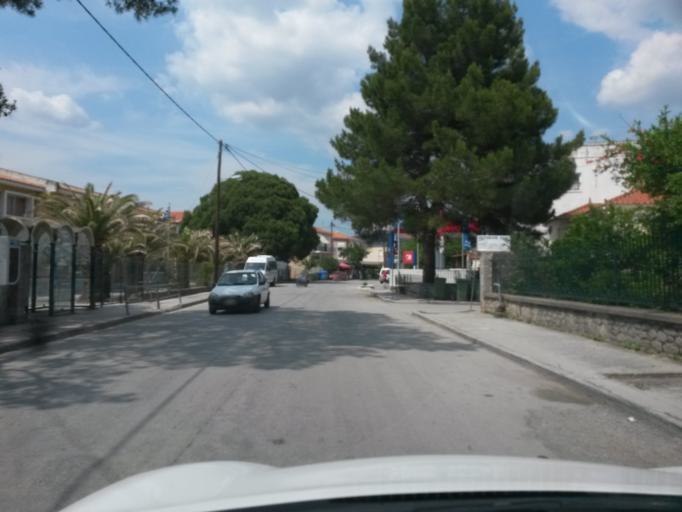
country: GR
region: North Aegean
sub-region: Nomos Lesvou
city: Kalloni
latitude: 39.2349
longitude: 26.2081
